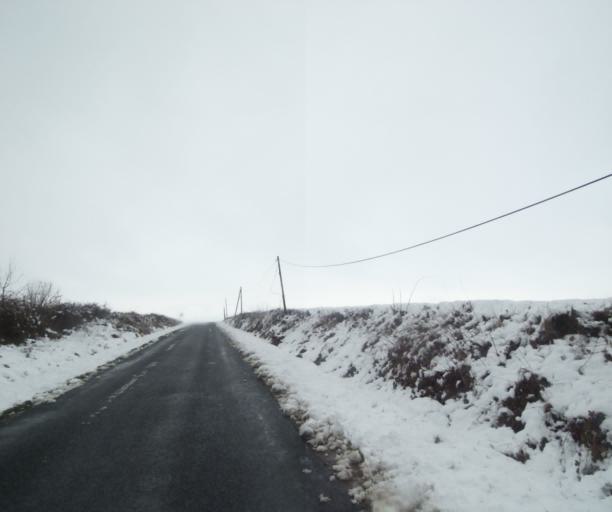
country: FR
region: Champagne-Ardenne
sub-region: Departement de la Haute-Marne
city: Montier-en-Der
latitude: 48.4626
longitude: 4.8238
